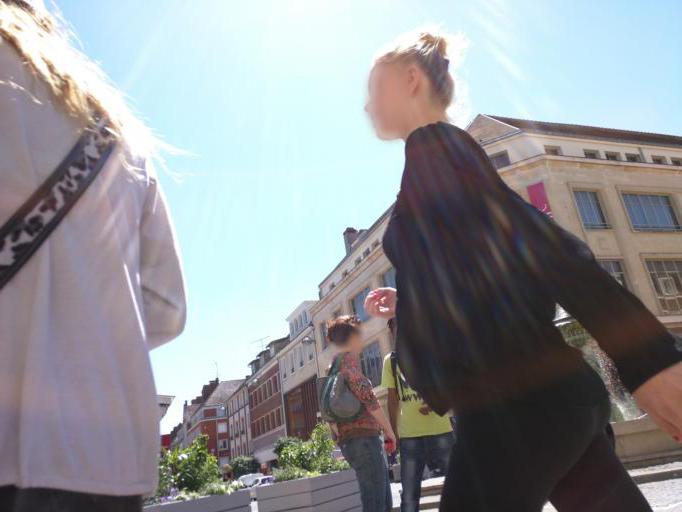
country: FR
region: Picardie
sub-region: Departement de l'Oise
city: Beauvais
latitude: 49.4313
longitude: 2.0836
